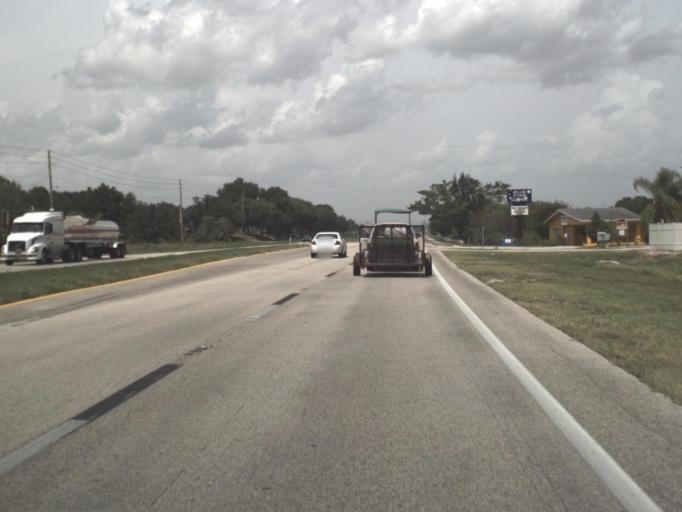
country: US
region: Florida
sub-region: Polk County
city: Lake Wales
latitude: 27.8882
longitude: -81.5996
